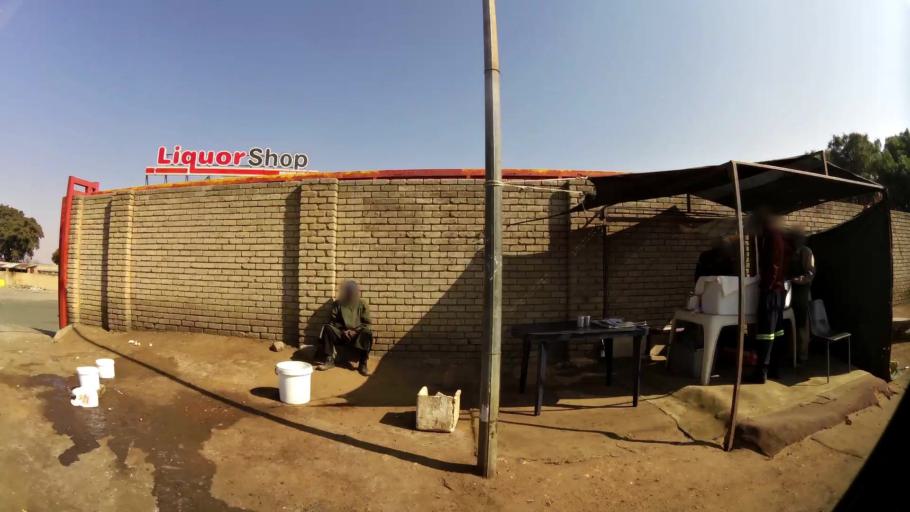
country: ZA
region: Gauteng
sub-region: City of Johannesburg Metropolitan Municipality
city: Soweto
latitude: -26.2441
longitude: 27.9410
